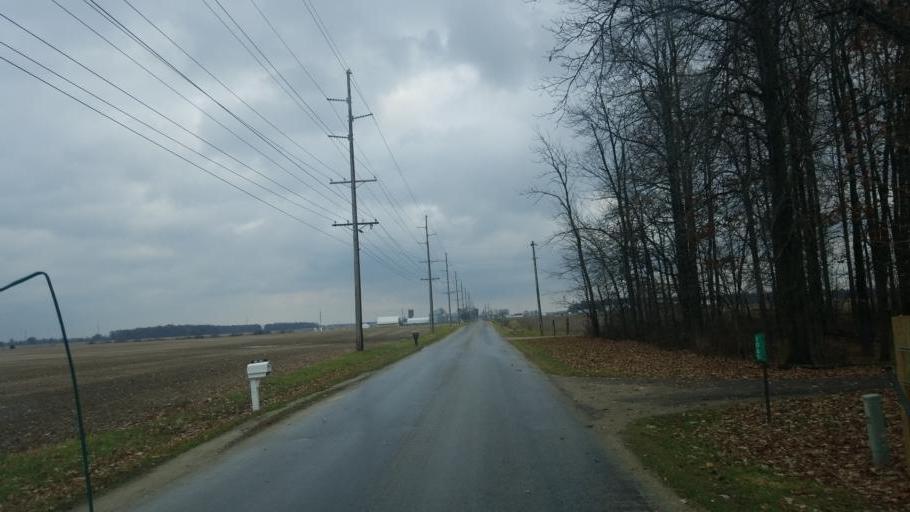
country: US
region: Indiana
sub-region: Jay County
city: Portland
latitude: 40.5123
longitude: -84.9605
